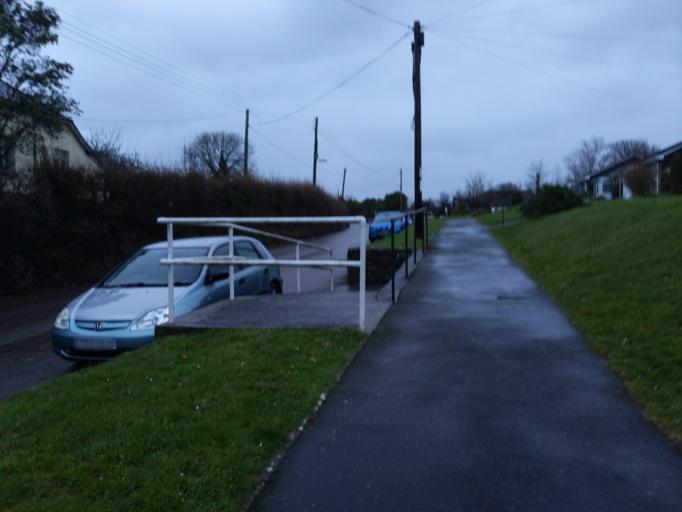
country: GB
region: England
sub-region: Devon
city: Wembury
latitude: 50.3181
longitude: -4.0355
